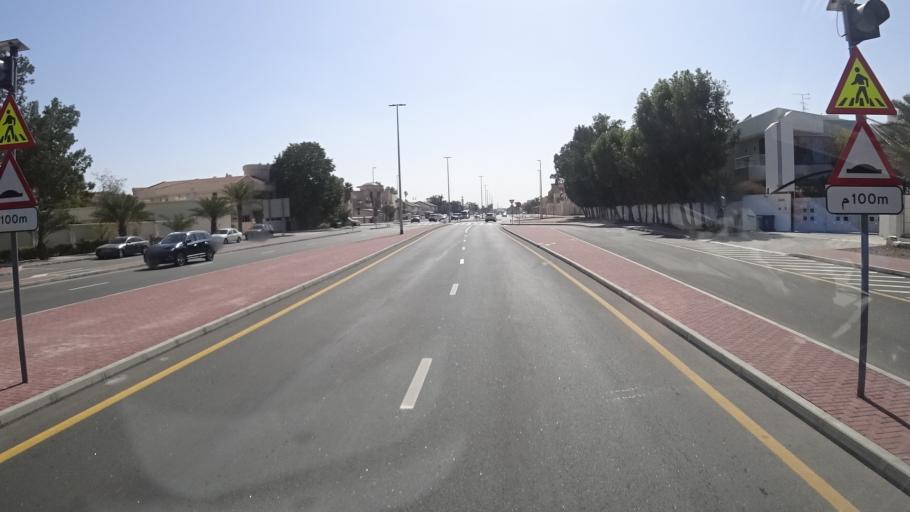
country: AE
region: Dubai
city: Dubai
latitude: 25.1590
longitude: 55.2094
